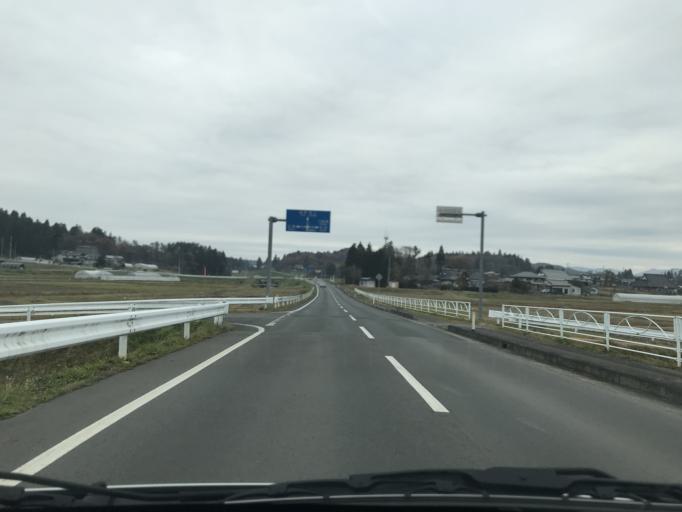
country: JP
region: Iwate
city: Mizusawa
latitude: 39.1880
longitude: 141.2221
